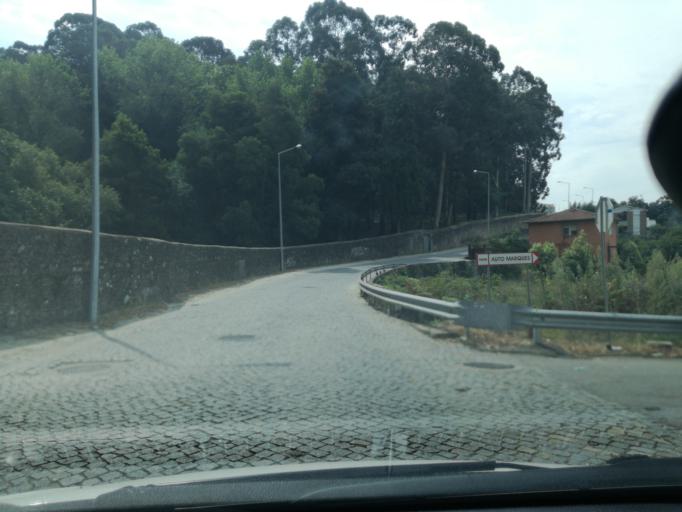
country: PT
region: Porto
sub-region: Vila Nova de Gaia
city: Grijo
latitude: 41.0337
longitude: -8.5879
